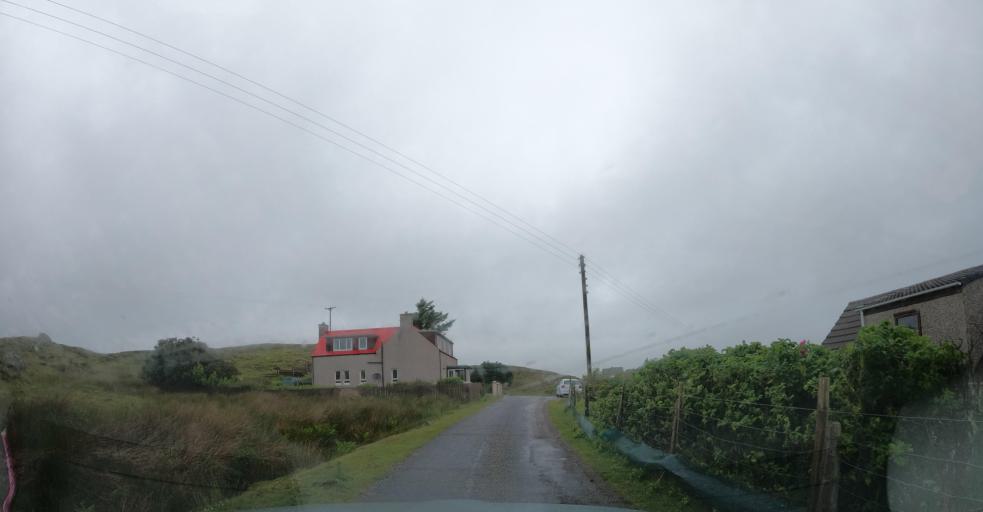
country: GB
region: Scotland
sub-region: Eilean Siar
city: Benbecula
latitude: 57.4883
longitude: -7.2218
